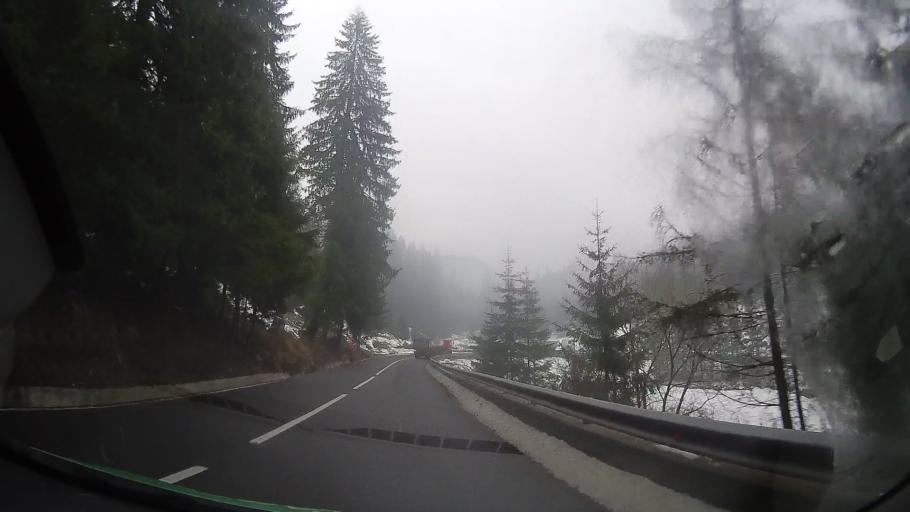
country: RO
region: Harghita
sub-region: Municipiul Gheorgheni
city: Gheorgheni
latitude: 46.7563
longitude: 25.7043
